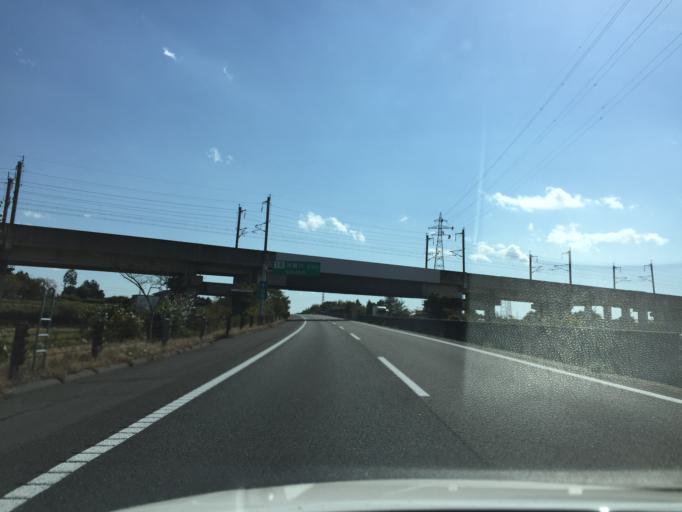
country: JP
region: Fukushima
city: Sukagawa
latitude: 37.3092
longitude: 140.3452
